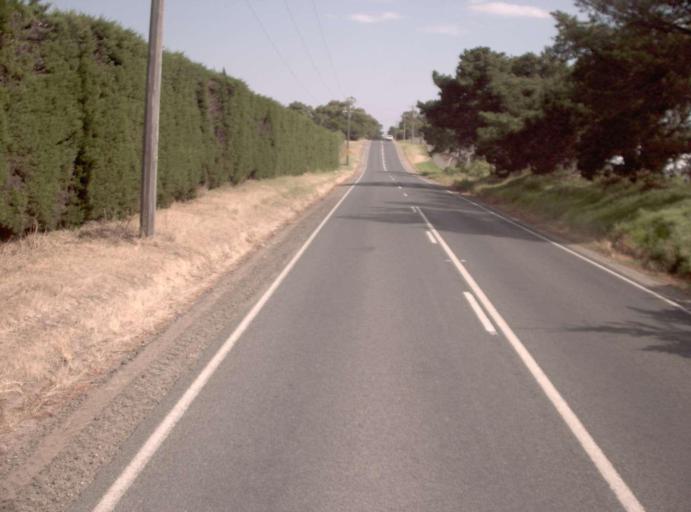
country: AU
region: Victoria
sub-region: Casey
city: Junction Village
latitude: -38.1504
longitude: 145.3207
